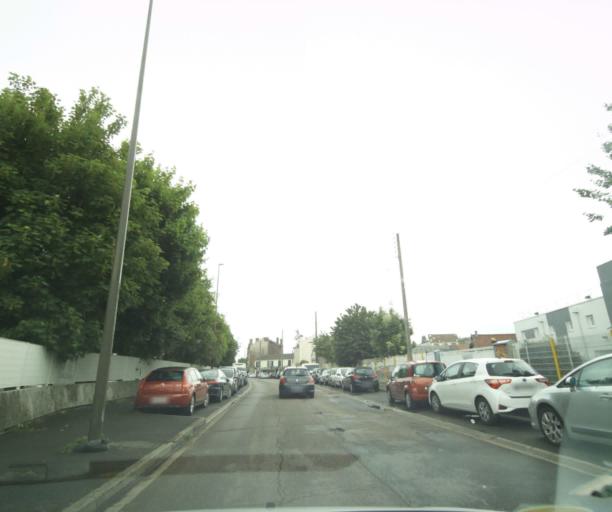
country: FR
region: Ile-de-France
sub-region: Departement du Val-d'Oise
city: Bezons
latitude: 48.9323
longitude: 2.2335
